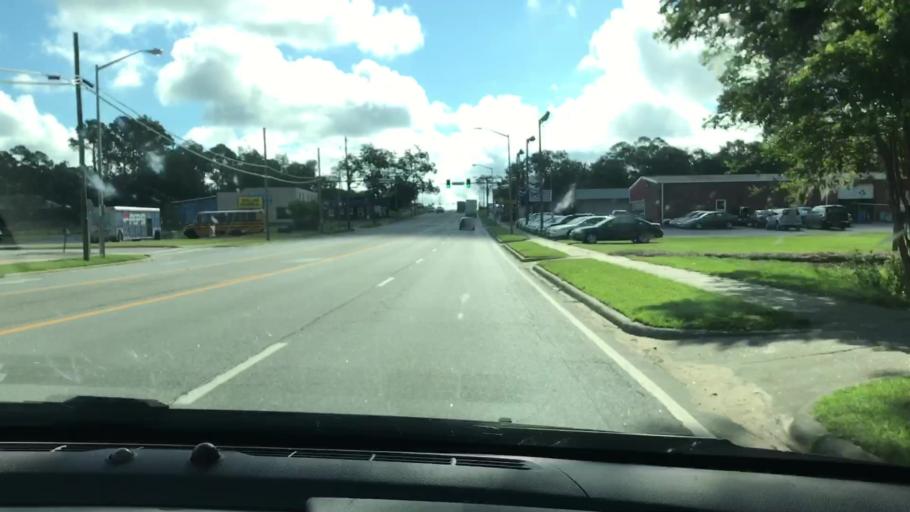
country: US
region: Georgia
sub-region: Worth County
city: Sylvester
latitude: 31.5308
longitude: -83.8428
